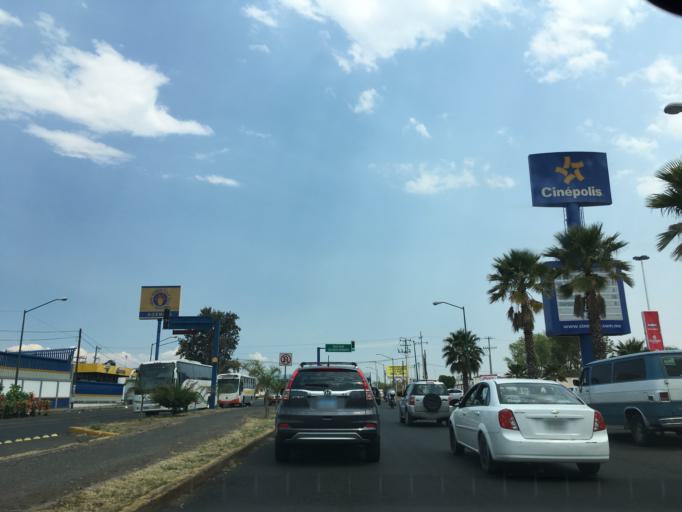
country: MX
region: Guanajuato
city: Moroleon
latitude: 20.1200
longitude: -101.1771
